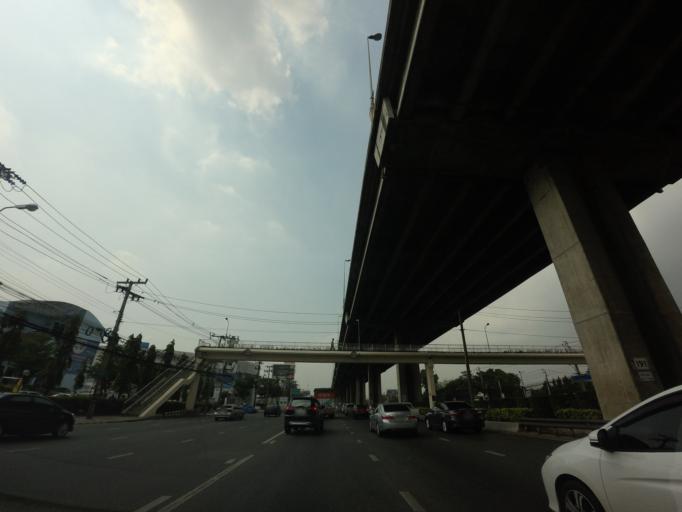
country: TH
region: Bangkok
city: Taling Chan
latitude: 13.7837
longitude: 100.4014
